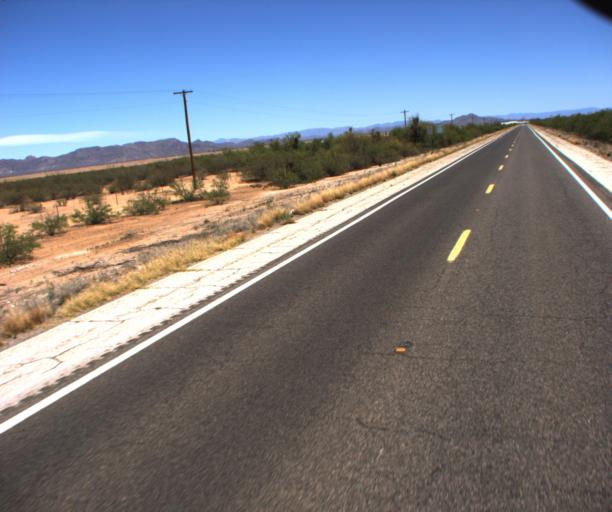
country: US
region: Arizona
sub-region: Yavapai County
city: Congress
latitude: 33.9331
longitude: -113.2109
